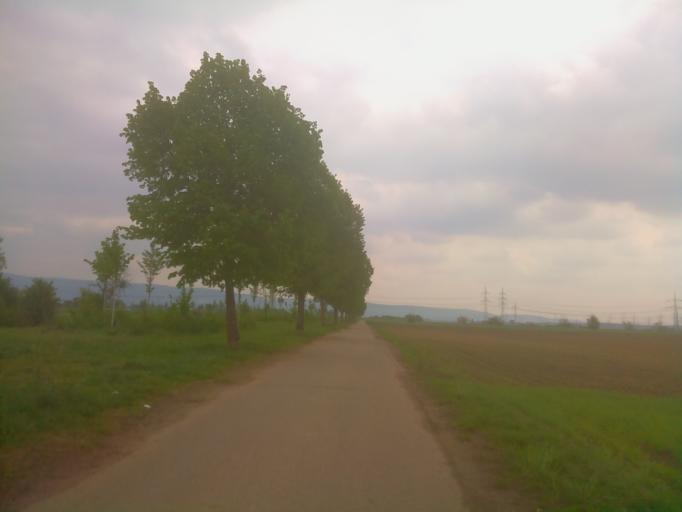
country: DE
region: Baden-Wuerttemberg
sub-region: Karlsruhe Region
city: Schwetzingen
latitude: 49.3782
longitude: 8.5963
